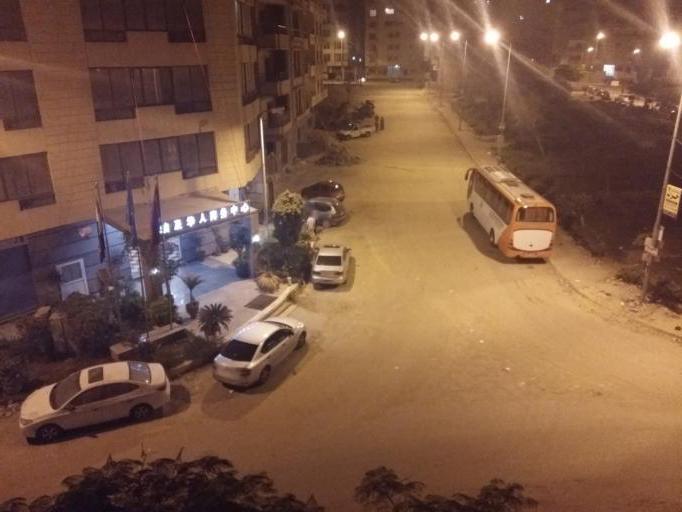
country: EG
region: Muhafazat al Qahirah
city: Cairo
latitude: 29.9836
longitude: 31.3092
